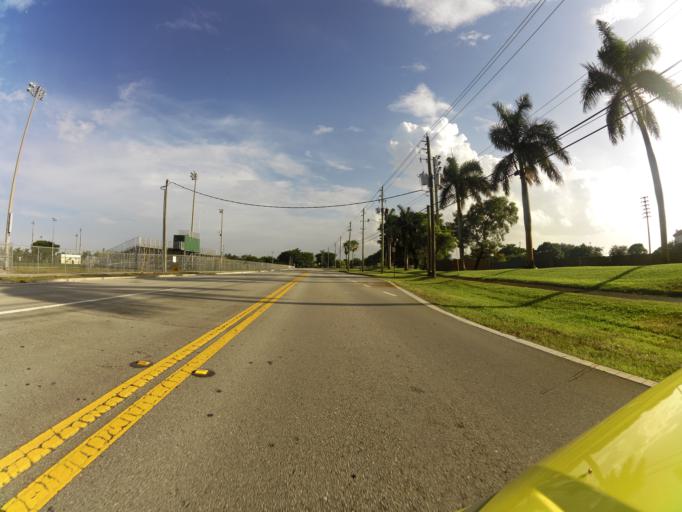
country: US
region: Florida
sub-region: Broward County
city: Davie
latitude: 26.0756
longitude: -80.2398
